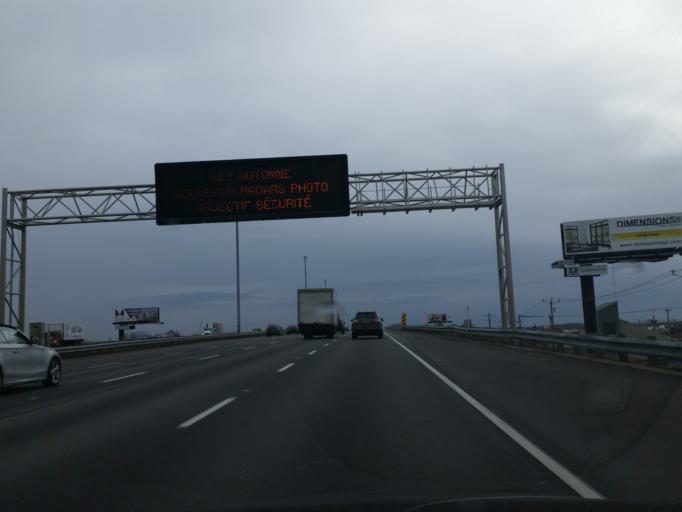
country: CA
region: Quebec
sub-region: Laurentides
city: Sainte-Therese
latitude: 45.6364
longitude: -73.8541
